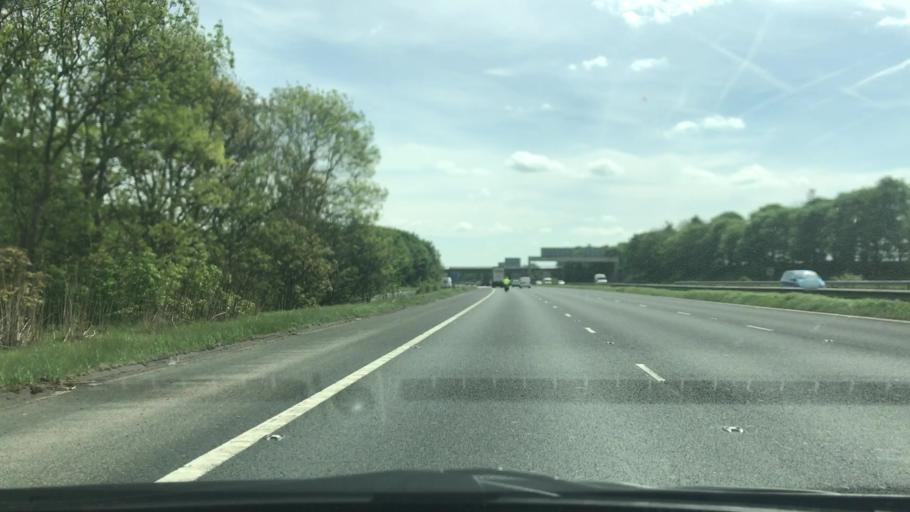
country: GB
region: England
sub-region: City and Borough of Wakefield
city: Knottingley
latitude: 53.6947
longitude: -1.2625
